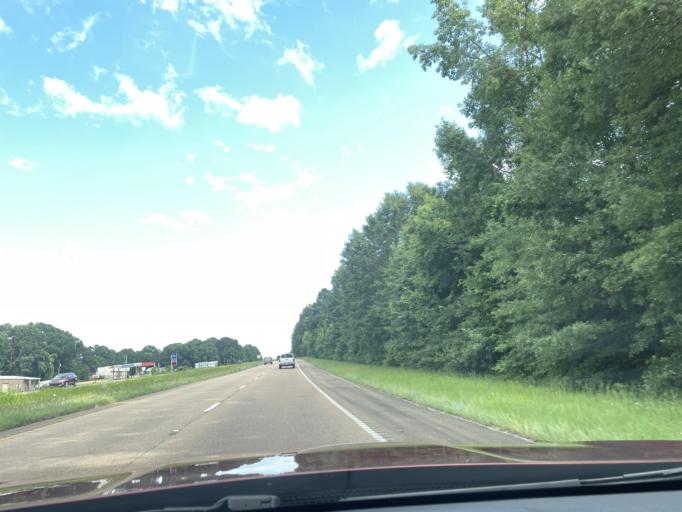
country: US
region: Mississippi
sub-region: Madison County
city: Flora
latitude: 32.5224
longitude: -90.3078
